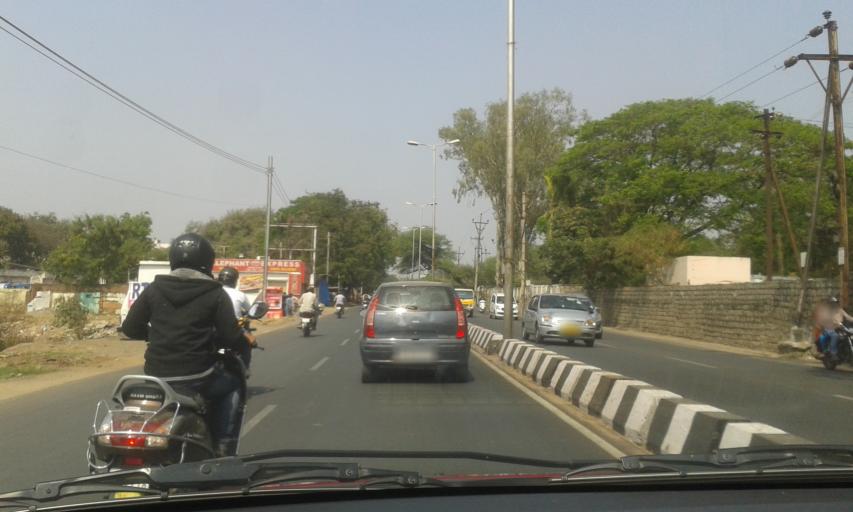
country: IN
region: Telangana
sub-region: Rangareddi
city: Secunderabad
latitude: 17.4960
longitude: 78.5130
